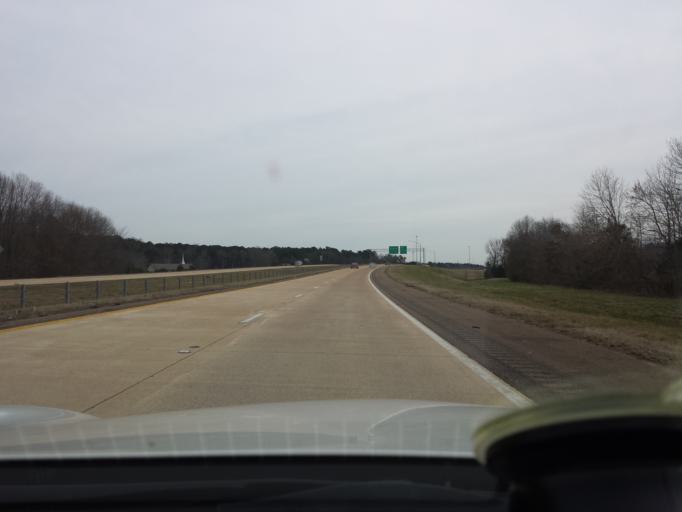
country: US
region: Mississippi
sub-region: Oktibbeha County
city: Starkville
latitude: 33.4937
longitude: -88.7958
